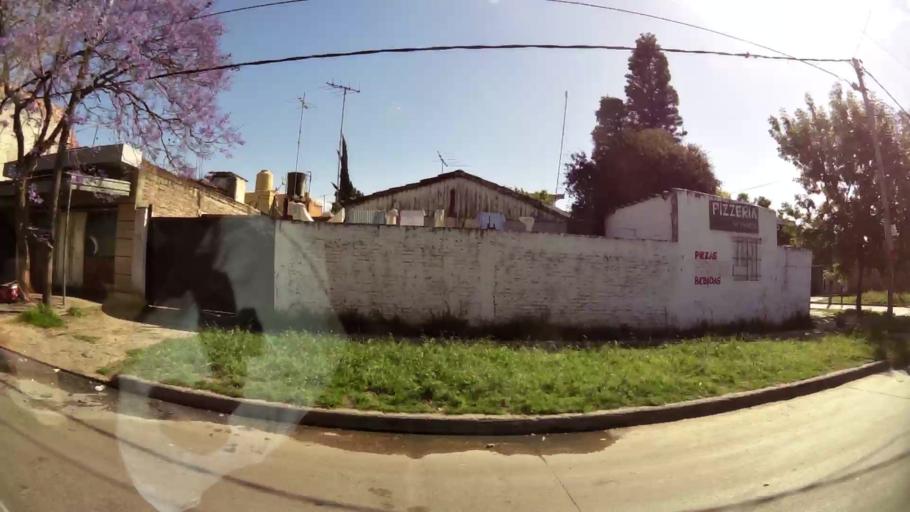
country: AR
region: Buenos Aires
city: Caseros
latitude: -34.5404
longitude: -58.5925
